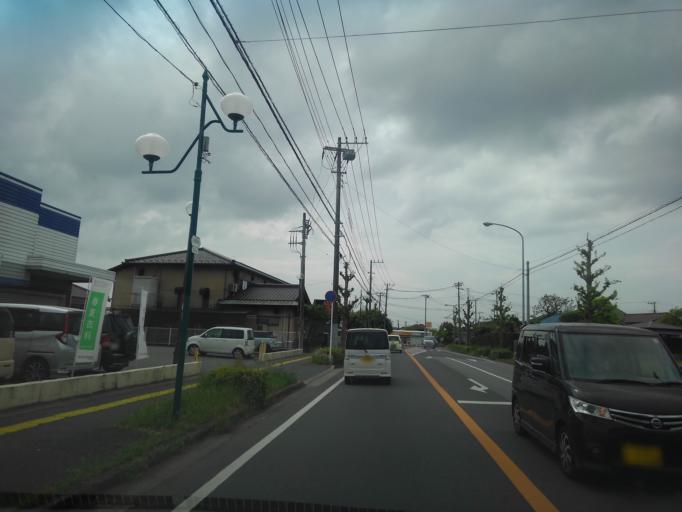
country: JP
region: Chiba
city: Kimitsu
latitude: 35.3294
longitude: 139.9218
